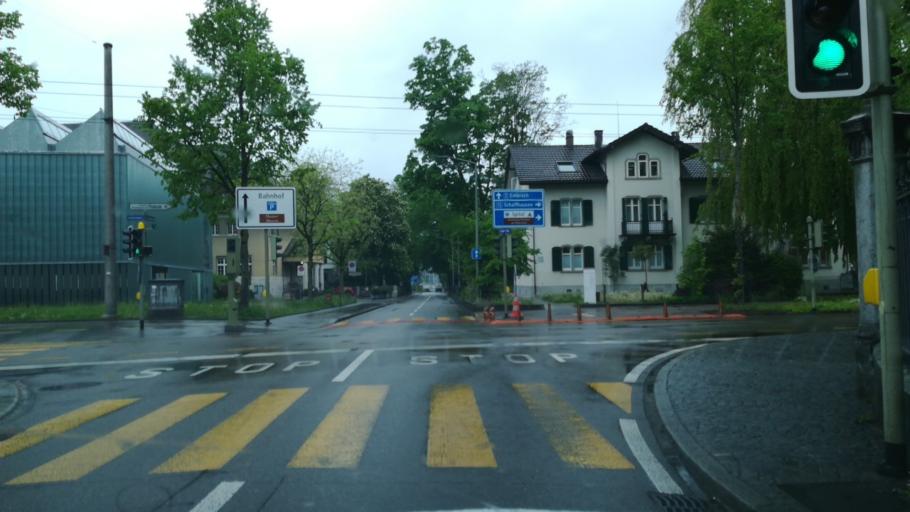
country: CH
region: Zurich
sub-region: Bezirk Winterthur
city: Stadt Winterthur (Kreis 1) / Altstadt
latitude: 47.5025
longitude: 8.7309
